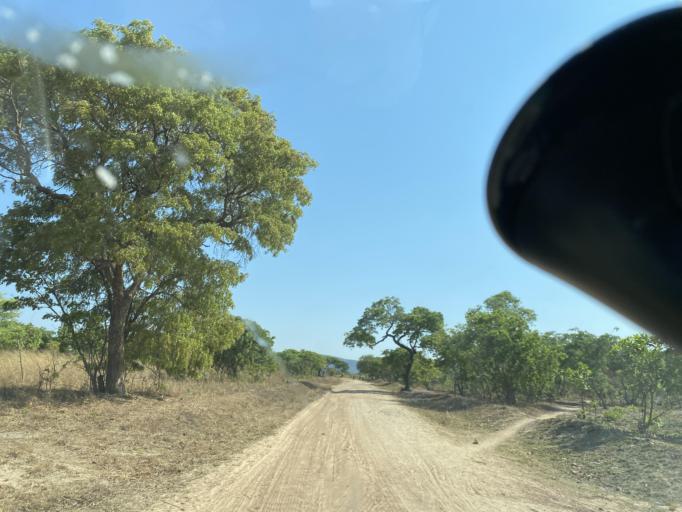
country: ZM
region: Lusaka
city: Chongwe
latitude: -15.2341
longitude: 28.8393
